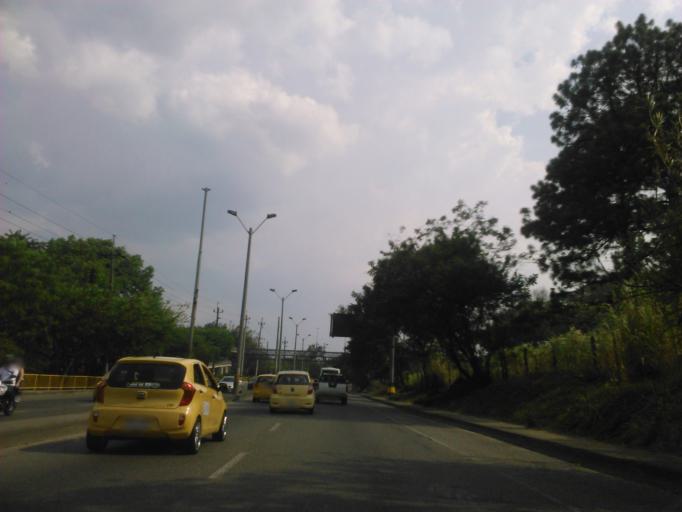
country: CO
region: Antioquia
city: Bello
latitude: 6.3065
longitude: -75.5605
